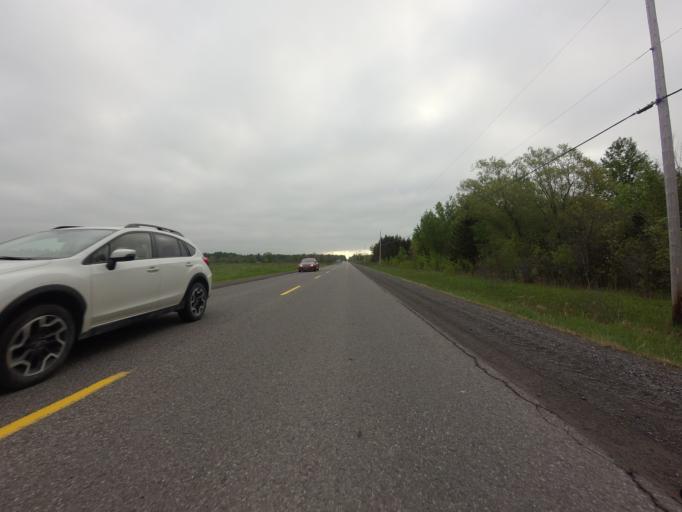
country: CA
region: Ontario
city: Ottawa
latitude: 45.3546
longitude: -75.5478
